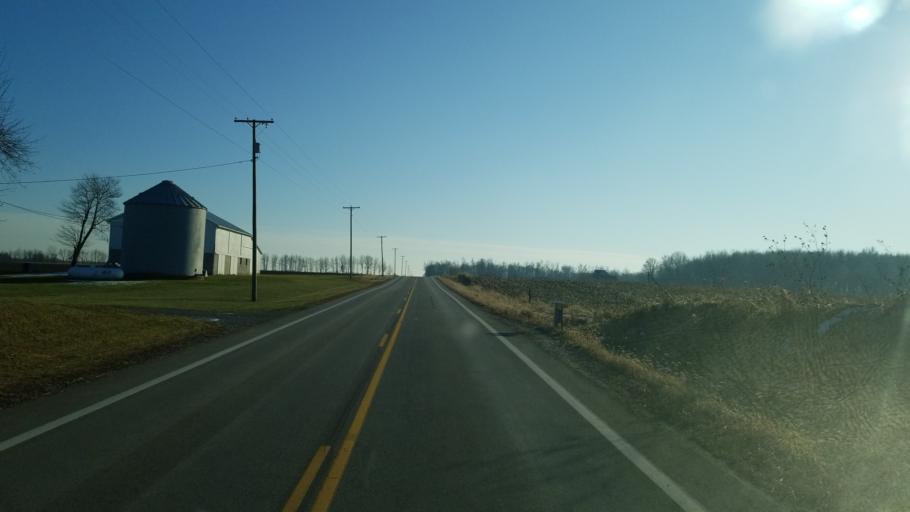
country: US
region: Ohio
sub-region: Seneca County
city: Tiffin
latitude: 41.0227
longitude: -83.0154
